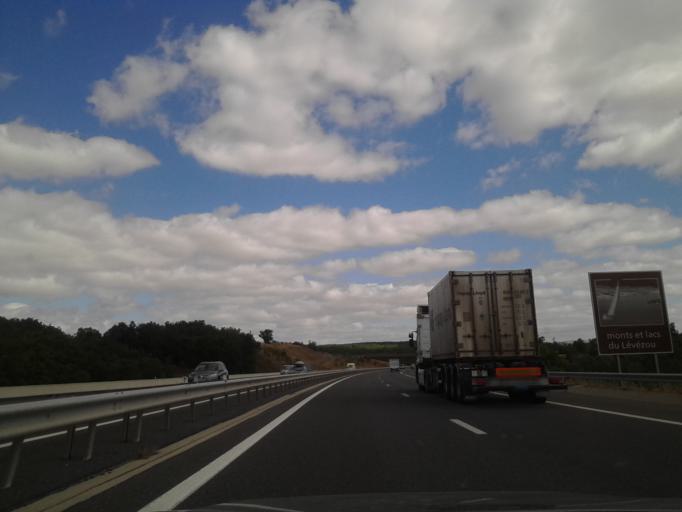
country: FR
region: Midi-Pyrenees
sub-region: Departement de l'Aveyron
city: Creissels
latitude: 44.1494
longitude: 3.0173
